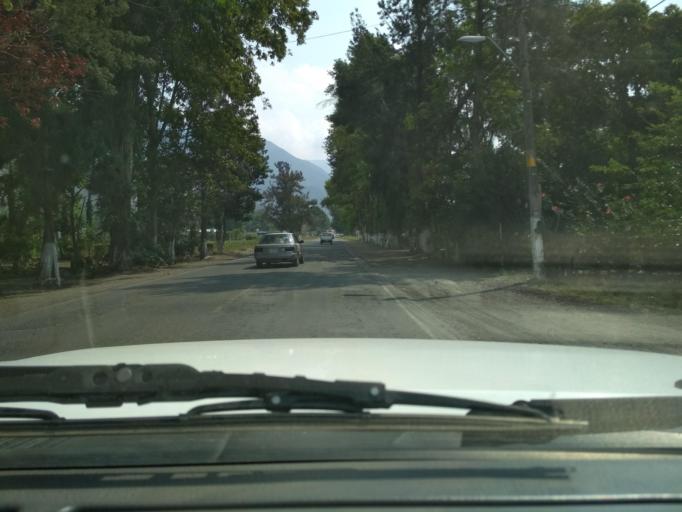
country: MX
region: Veracruz
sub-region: Acultzingo
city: Sierra de Agua
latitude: 18.7551
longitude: -97.2342
